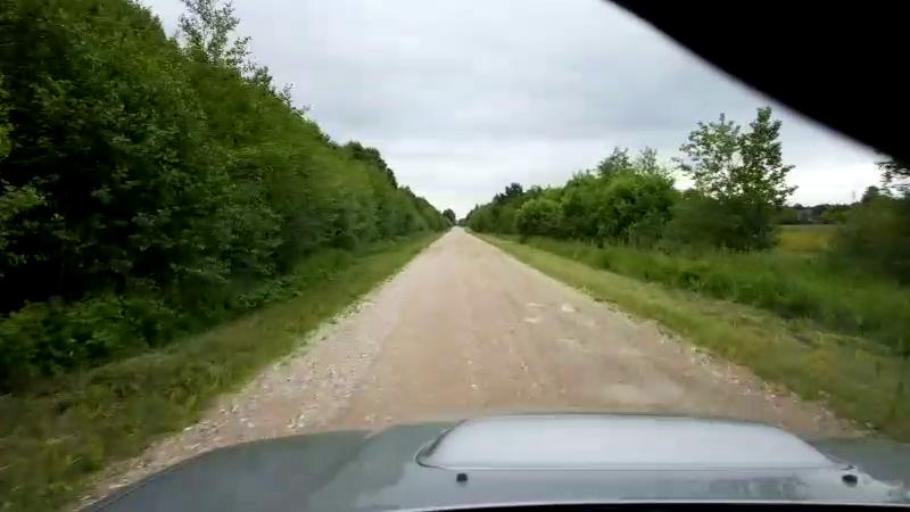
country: EE
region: Paernumaa
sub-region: Halinga vald
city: Parnu-Jaagupi
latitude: 58.5494
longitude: 24.5608
